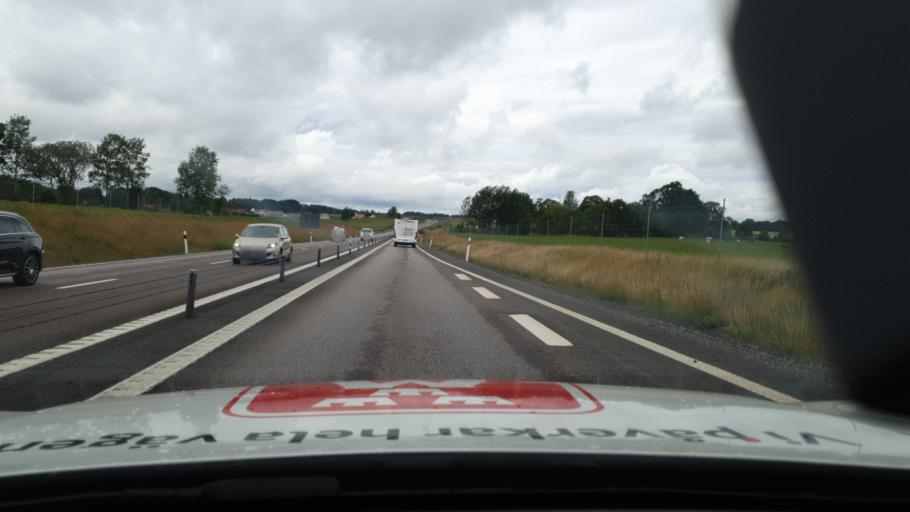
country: SE
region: Joenkoeping
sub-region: Jonkopings Kommun
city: Tenhult
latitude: 57.7352
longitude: 14.3073
